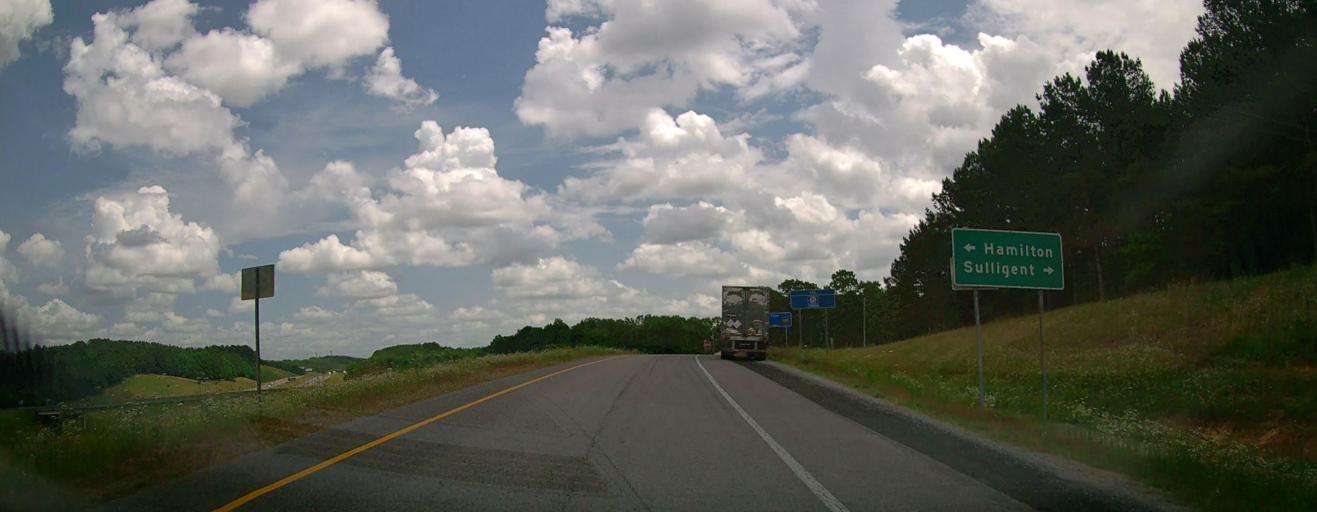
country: US
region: Alabama
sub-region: Marion County
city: Hamilton
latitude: 34.1207
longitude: -88.0478
